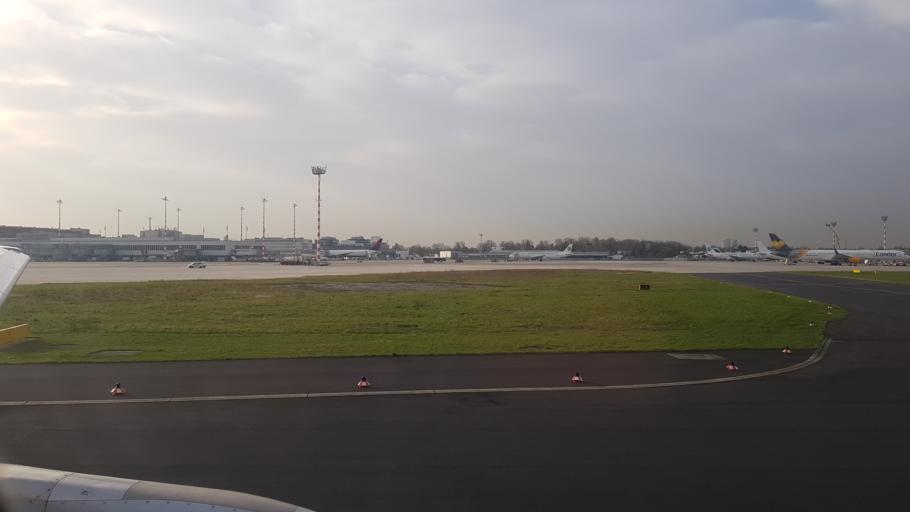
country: DE
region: North Rhine-Westphalia
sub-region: Regierungsbezirk Dusseldorf
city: Dusseldorf
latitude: 51.2795
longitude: 6.7563
